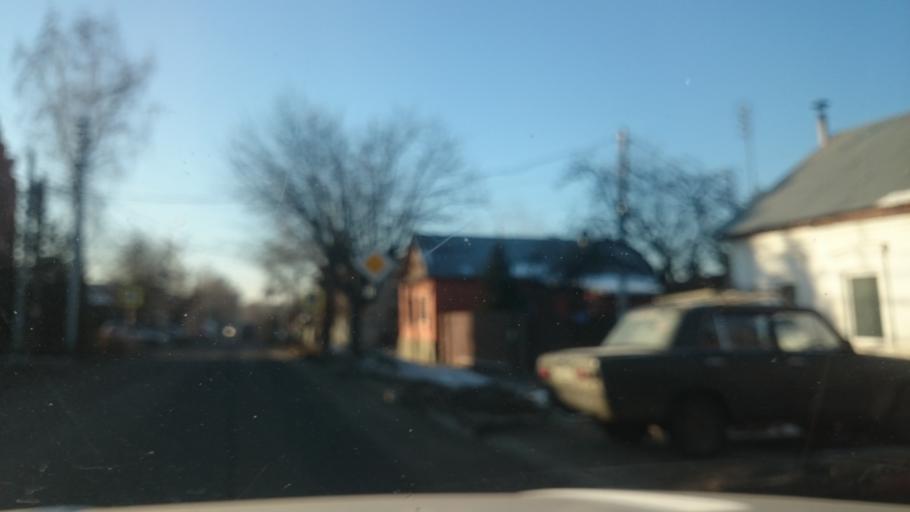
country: RU
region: Tula
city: Tula
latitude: 54.2043
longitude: 37.6376
